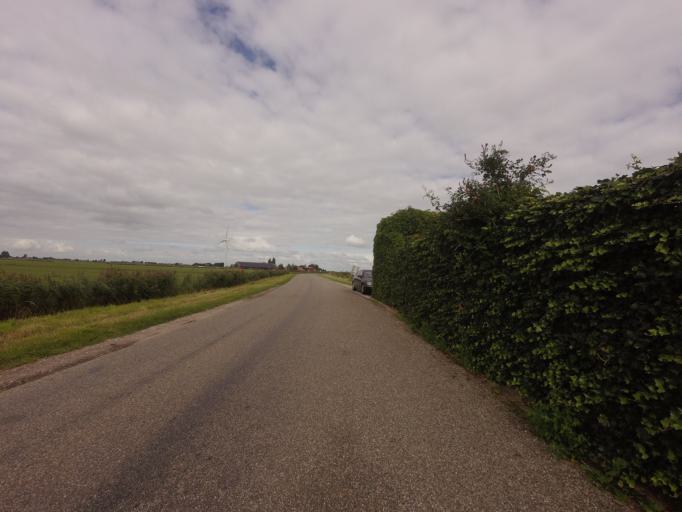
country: NL
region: Friesland
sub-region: Sudwest Fryslan
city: Workum
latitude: 52.9803
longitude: 5.4653
